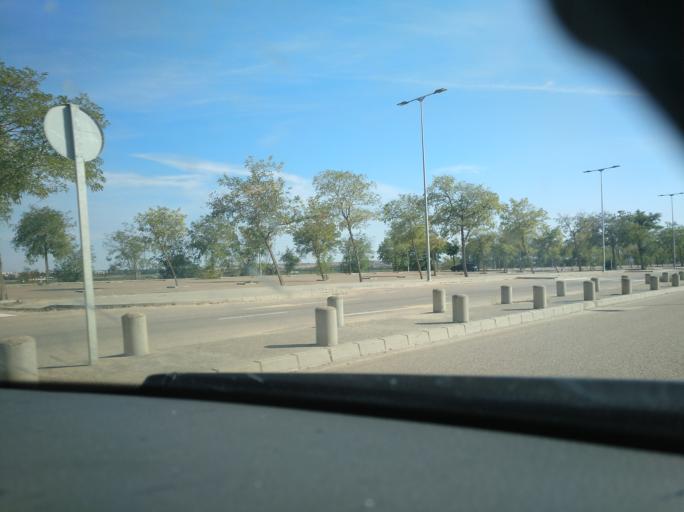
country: ES
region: Extremadura
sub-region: Provincia de Badajoz
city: Badajoz
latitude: 38.8810
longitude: -7.0253
